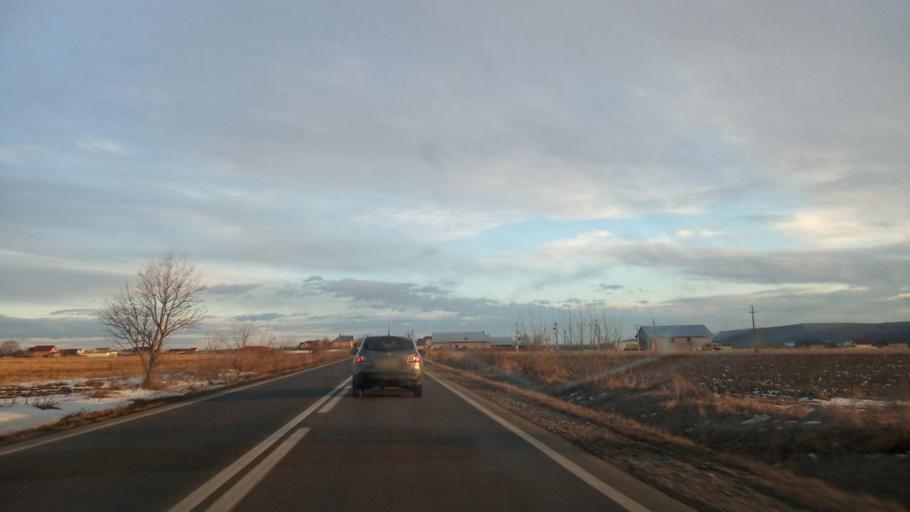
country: RO
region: Neamt
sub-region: Comuna Botesti
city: Nisiporesti
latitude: 47.0831
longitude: 26.7215
